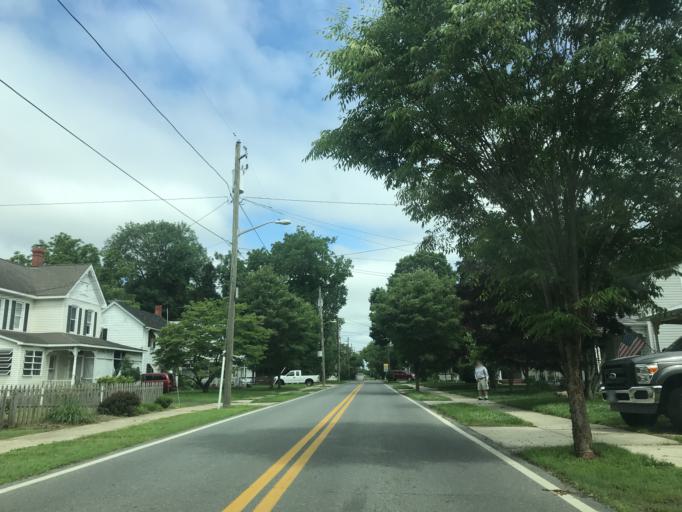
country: US
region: Maryland
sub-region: Caroline County
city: Ridgely
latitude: 38.9182
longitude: -75.9534
